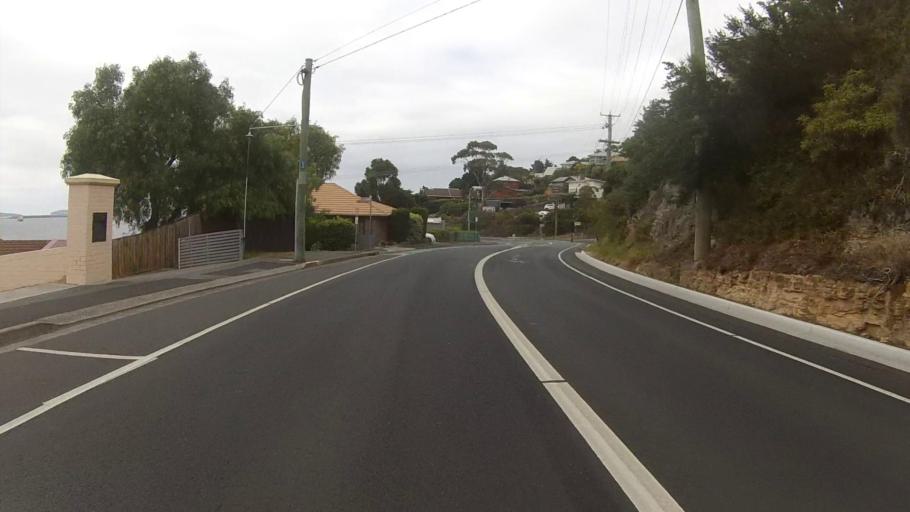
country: AU
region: Tasmania
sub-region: Kingborough
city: Taroona
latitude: -42.9237
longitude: 147.3604
